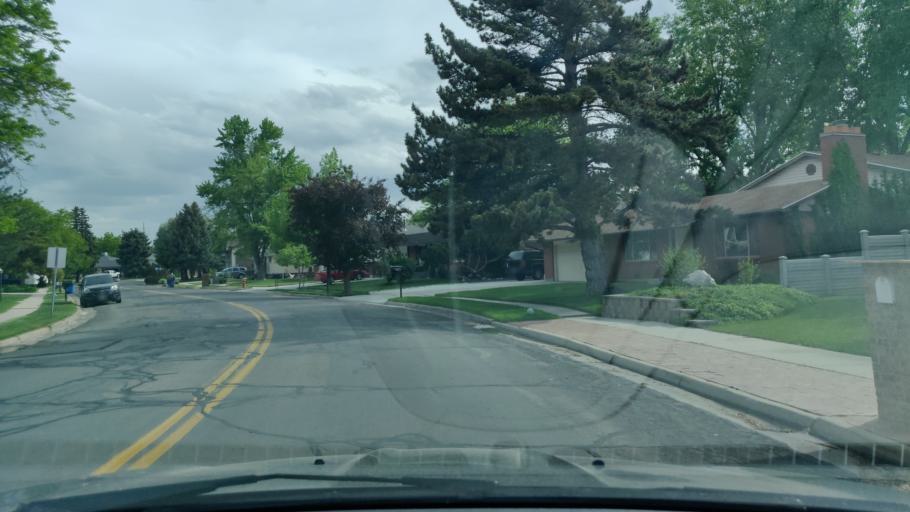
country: US
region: Utah
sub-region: Salt Lake County
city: Little Cottonwood Creek Valley
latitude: 40.6295
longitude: -111.8529
